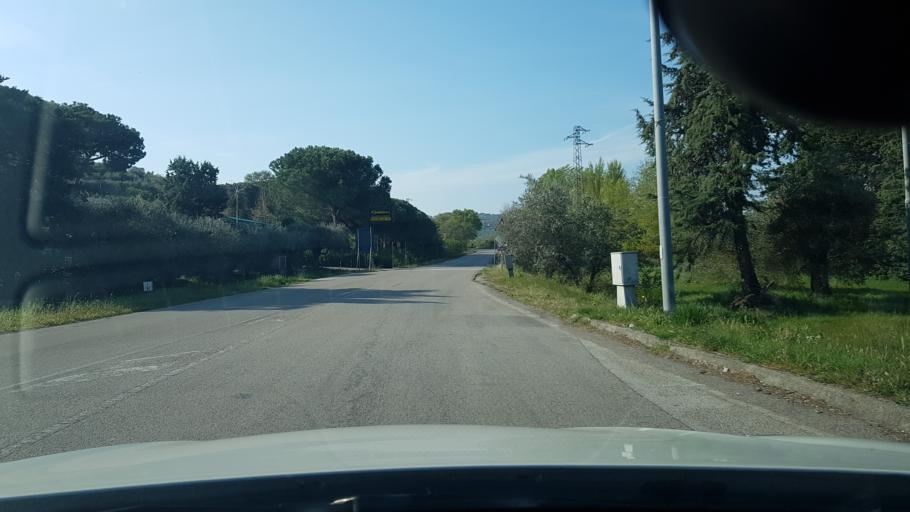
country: IT
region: Umbria
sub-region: Provincia di Perugia
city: Magione
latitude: 43.1684
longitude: 12.1898
